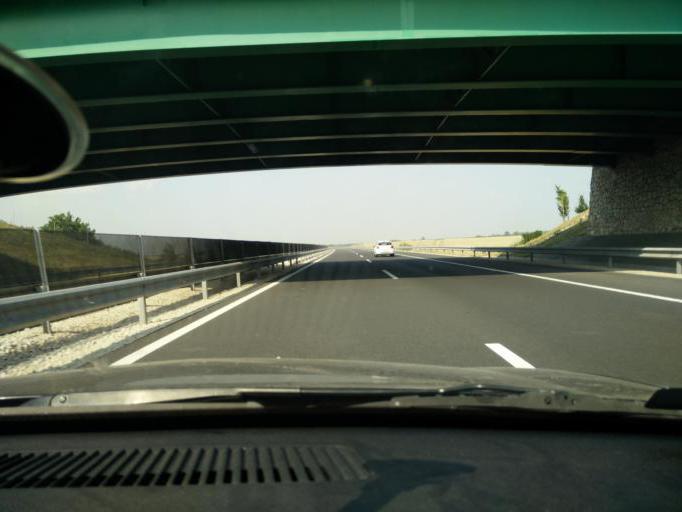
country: HU
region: Tolna
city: Tengelic
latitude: 46.4897
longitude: 18.7544
